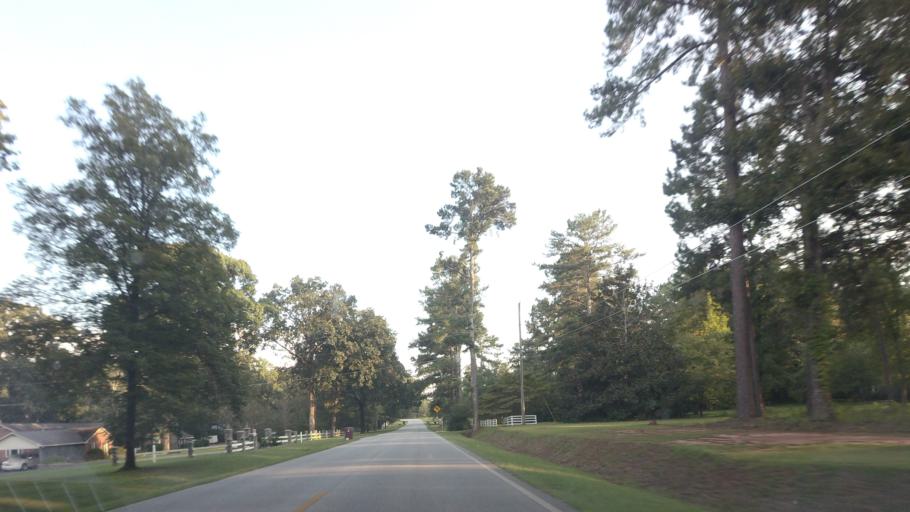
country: US
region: Georgia
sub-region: Bibb County
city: West Point
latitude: 32.8924
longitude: -83.7997
